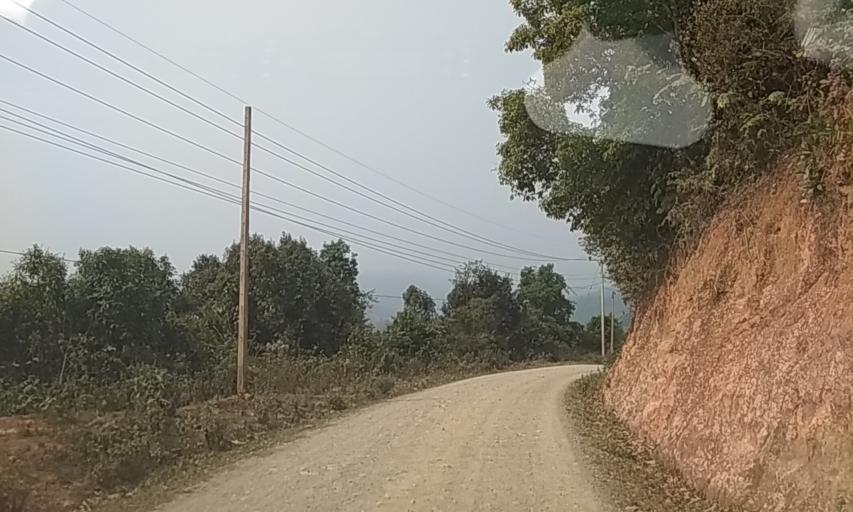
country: TH
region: Nan
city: Chaloem Phra Kiat
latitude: 20.0173
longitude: 101.1087
